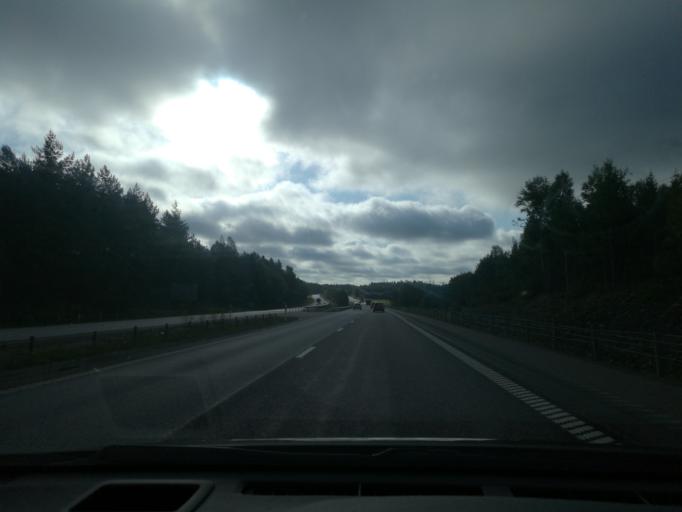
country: SE
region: Uppsala
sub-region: Habo Kommun
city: Balsta
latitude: 59.5584
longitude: 17.5767
